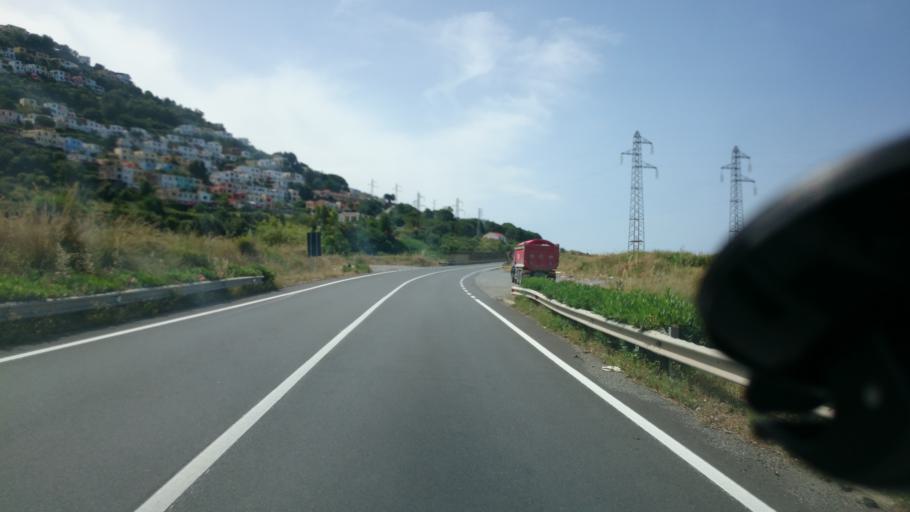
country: IT
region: Calabria
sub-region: Provincia di Cosenza
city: Praia a Mare
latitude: 39.8693
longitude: 15.7959
